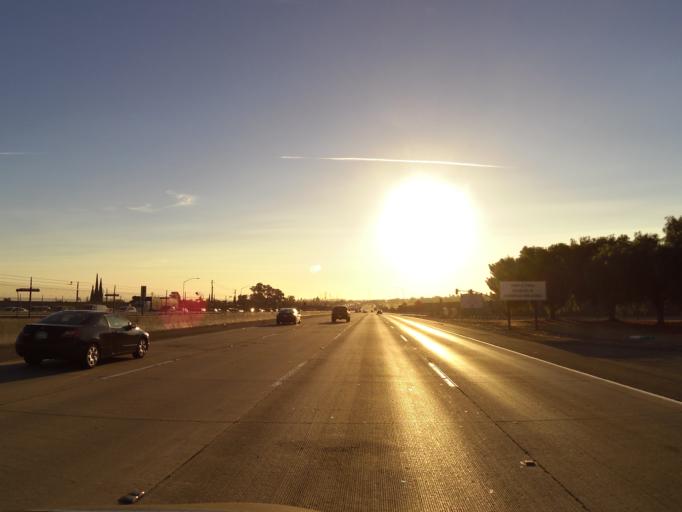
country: US
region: California
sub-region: Contra Costa County
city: Bay Point
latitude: 38.0185
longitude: -121.9406
